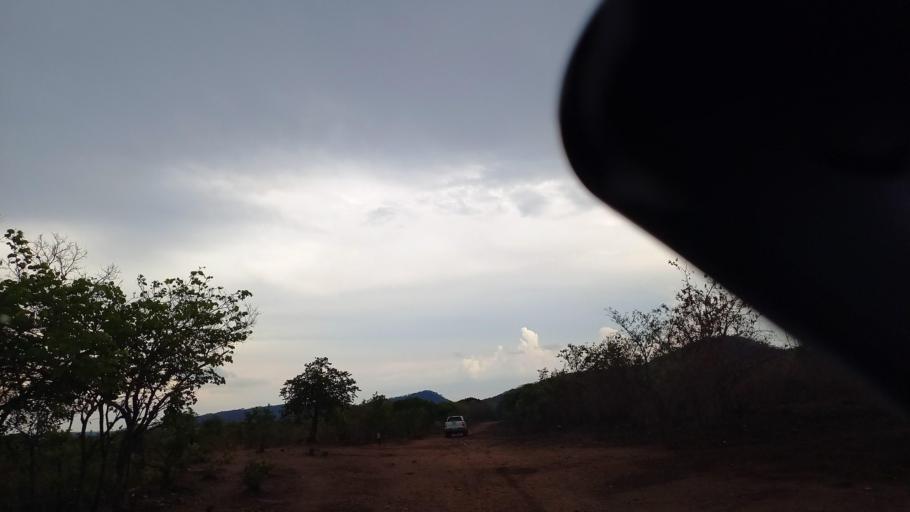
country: ZM
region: Lusaka
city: Kafue
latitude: -16.0262
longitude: 28.2985
